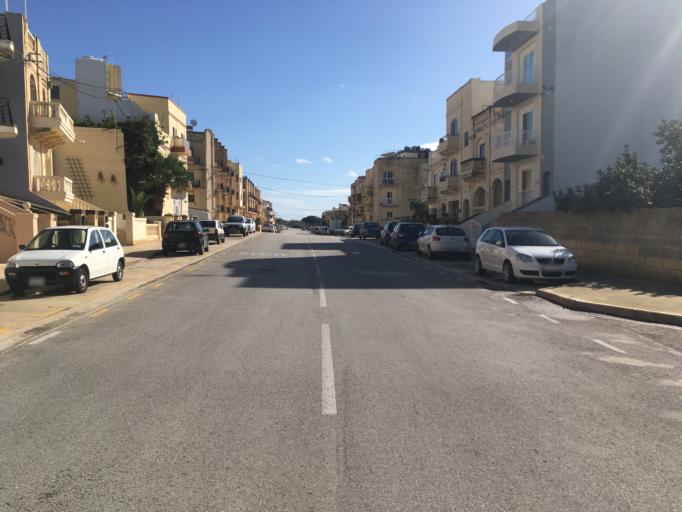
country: MT
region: Il-Mosta
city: Mosta
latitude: 35.9098
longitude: 14.4319
